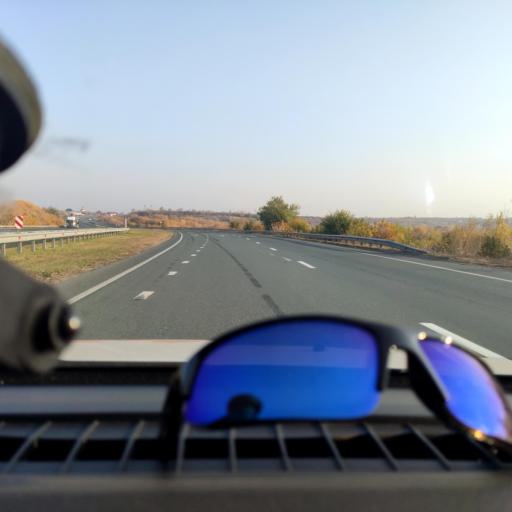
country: RU
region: Samara
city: Novokuybyshevsk
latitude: 53.0568
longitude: 50.0183
